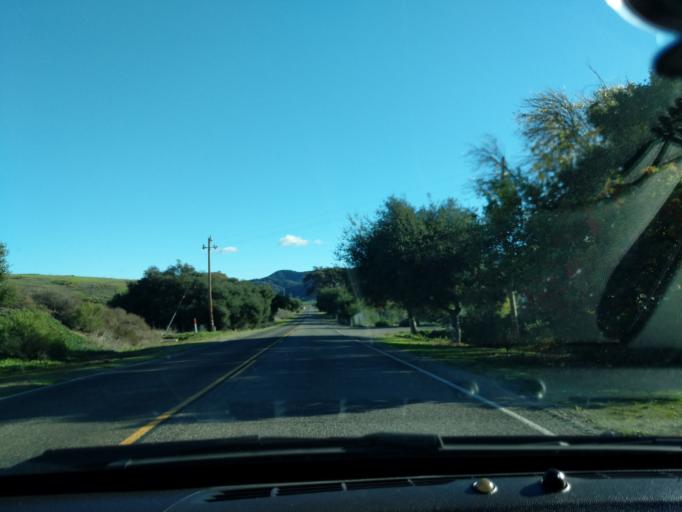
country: US
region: California
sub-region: Santa Barbara County
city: Los Alamos
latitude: 34.7538
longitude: -120.2942
